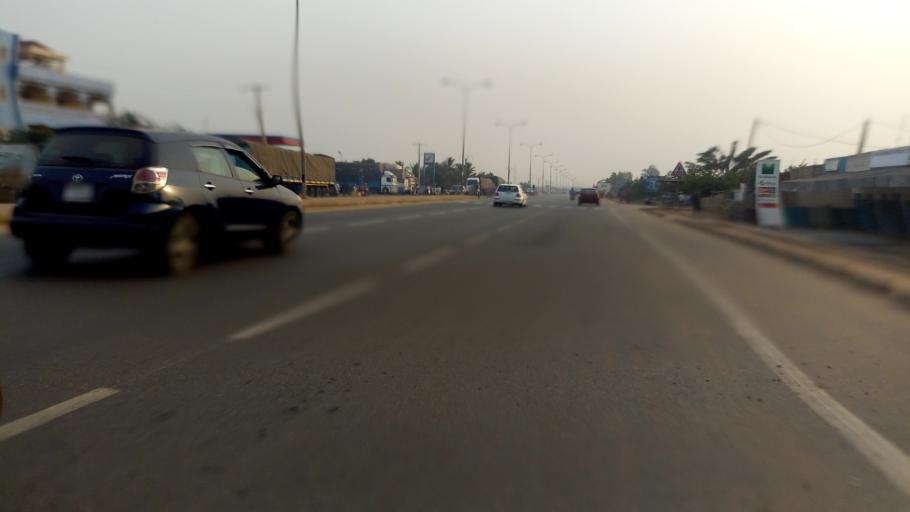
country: TG
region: Maritime
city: Lome
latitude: 6.2742
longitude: 1.2106
